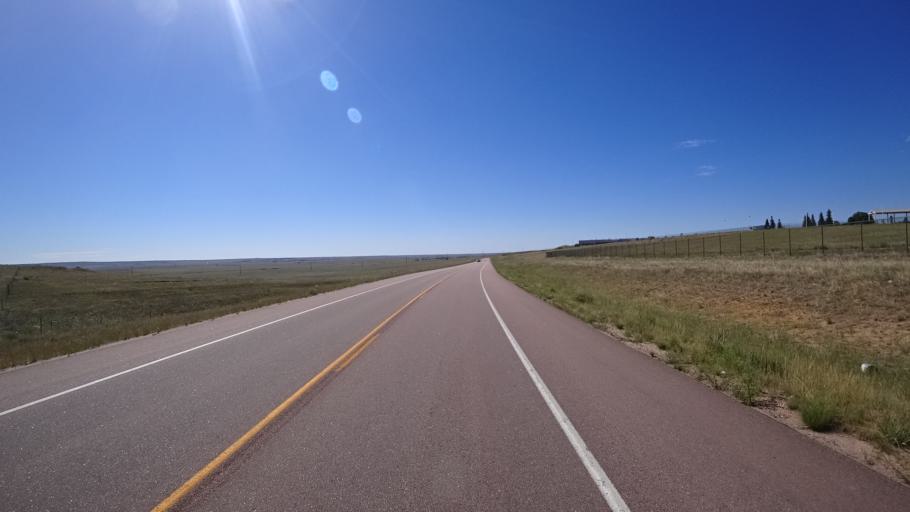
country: US
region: Colorado
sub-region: El Paso County
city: Cimarron Hills
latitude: 38.8192
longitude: -104.6780
